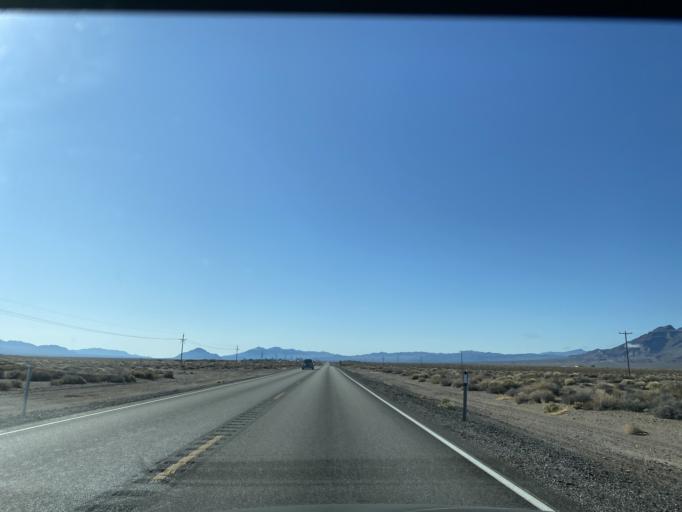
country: US
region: Nevada
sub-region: Nye County
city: Pahrump
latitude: 36.4395
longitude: -116.4221
